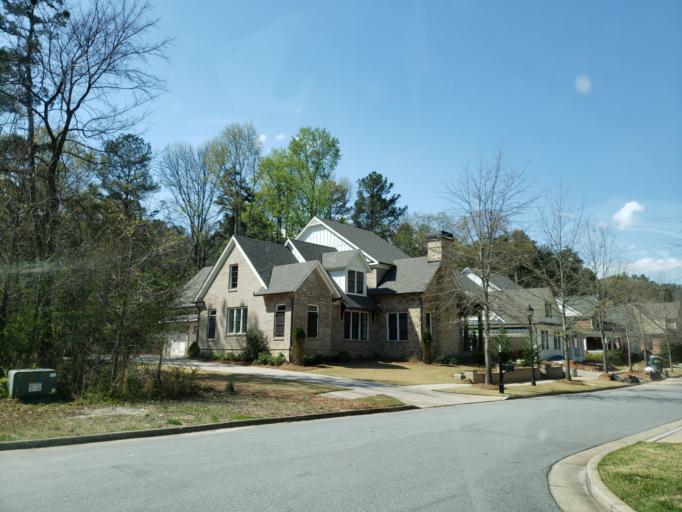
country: US
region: Georgia
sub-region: Cobb County
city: Marietta
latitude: 33.9759
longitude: -84.5690
